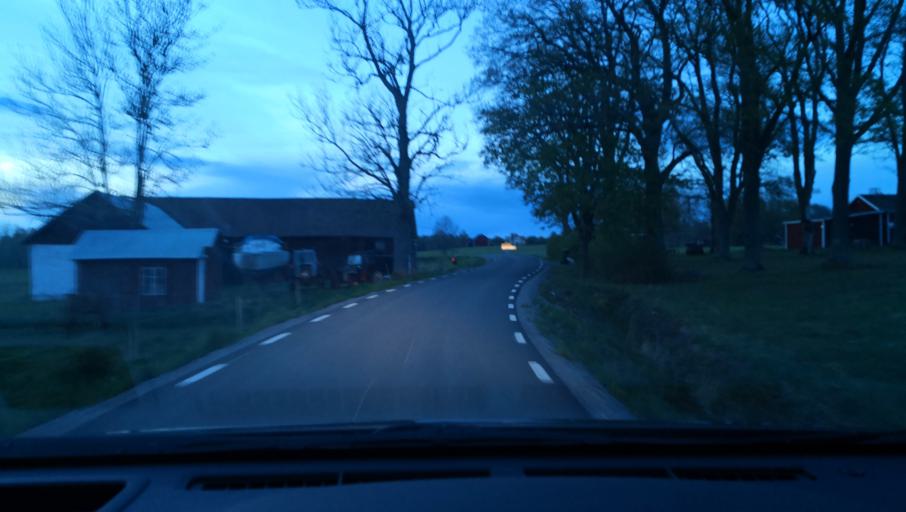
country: SE
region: OErebro
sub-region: Askersunds Kommun
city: Asbro
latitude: 59.0647
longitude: 14.9508
